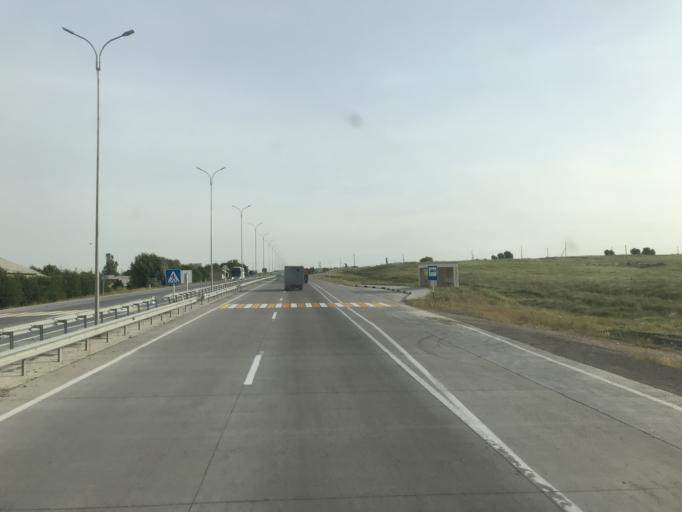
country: UZ
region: Toshkent
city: Qibray
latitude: 41.5623
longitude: 69.4083
